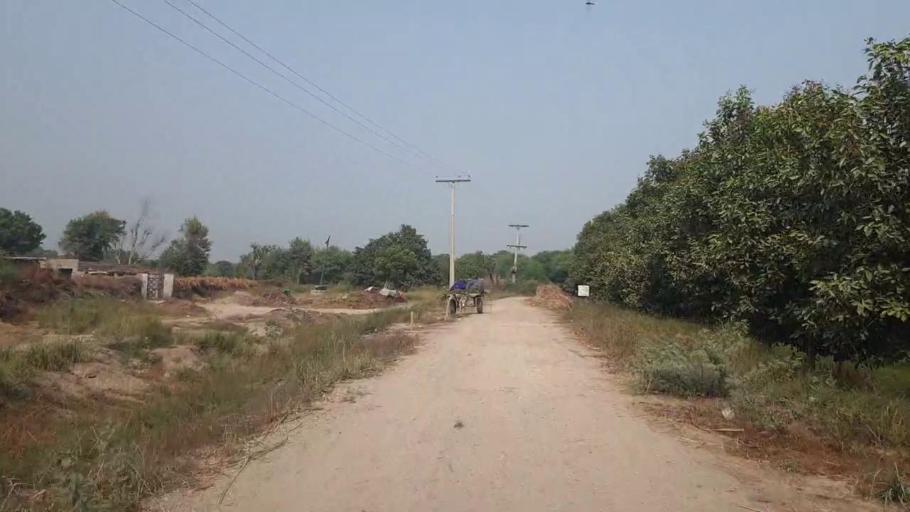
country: PK
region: Sindh
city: Tando Muhammad Khan
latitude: 25.2712
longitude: 68.5793
